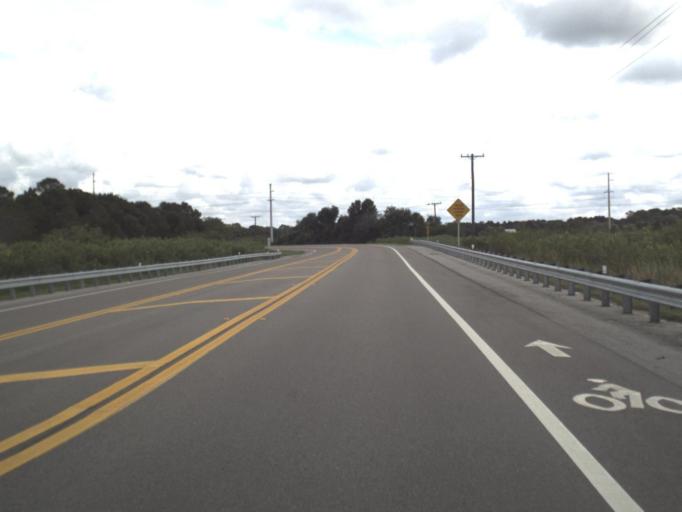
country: US
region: Florida
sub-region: Sarasota County
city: Lake Sarasota
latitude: 27.2456
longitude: -82.3760
